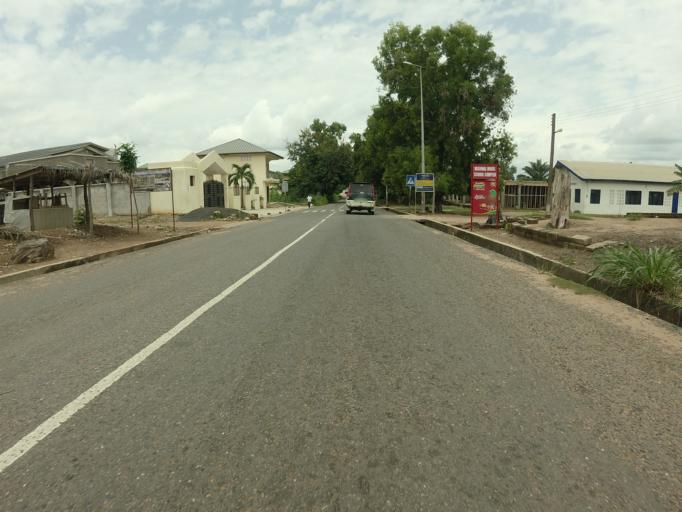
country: GH
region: Volta
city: Ho
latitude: 6.5997
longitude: 0.4624
